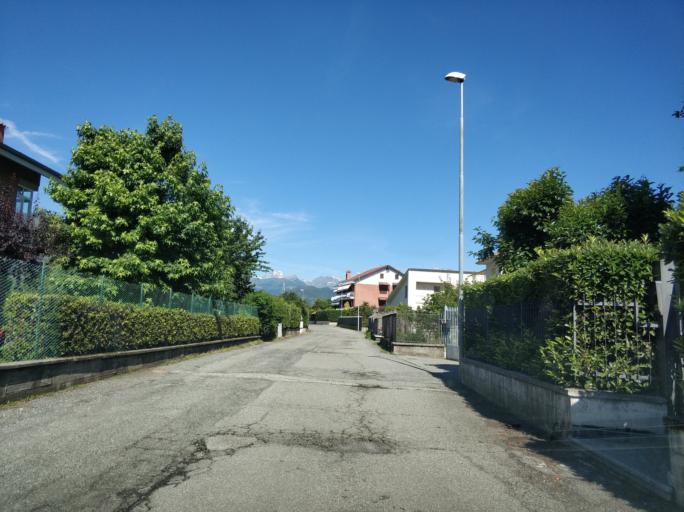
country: IT
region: Piedmont
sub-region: Provincia di Torino
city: Mathi
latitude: 45.2586
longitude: 7.5360
